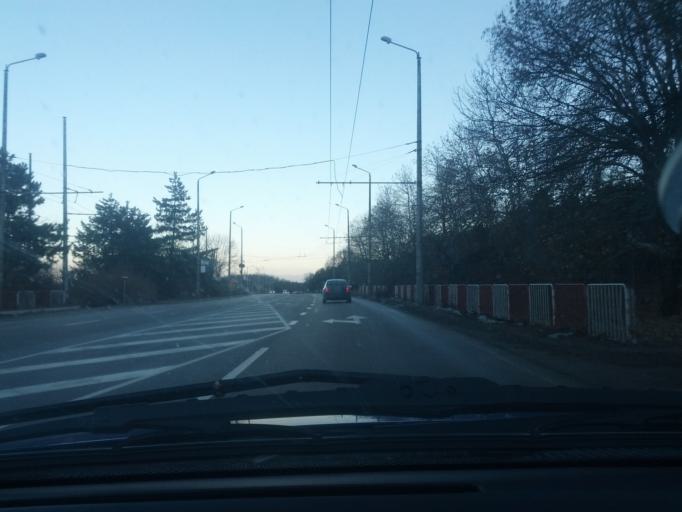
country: BG
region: Vratsa
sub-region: Obshtina Vratsa
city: Vratsa
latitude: 43.1857
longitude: 23.5840
